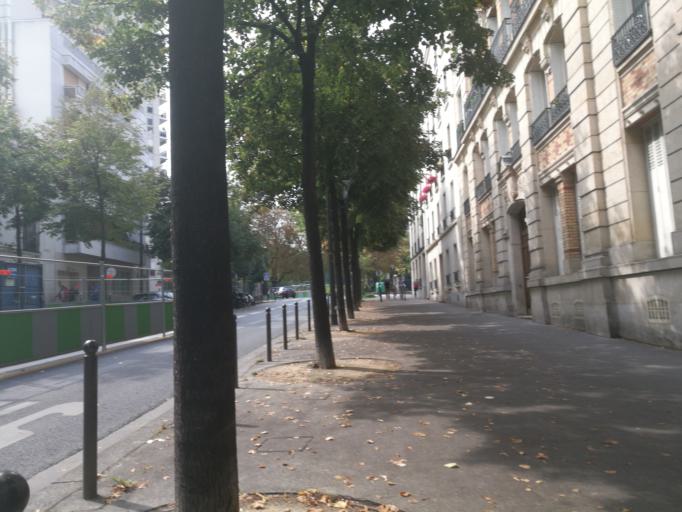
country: FR
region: Ile-de-France
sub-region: Departement du Val-de-Marne
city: Gentilly
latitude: 48.8251
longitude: 2.3403
